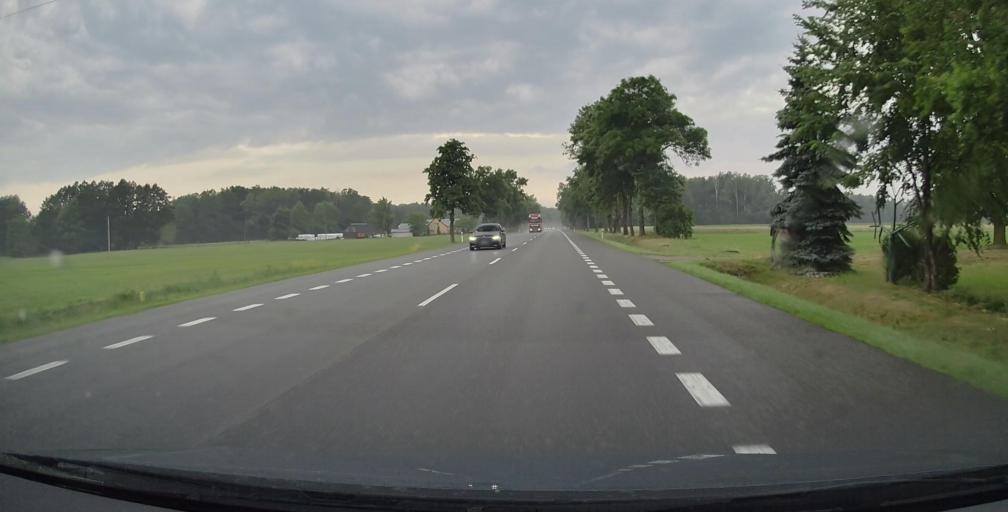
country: PL
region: Masovian Voivodeship
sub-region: Powiat siedlecki
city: Zbuczyn
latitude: 52.0748
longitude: 22.4990
